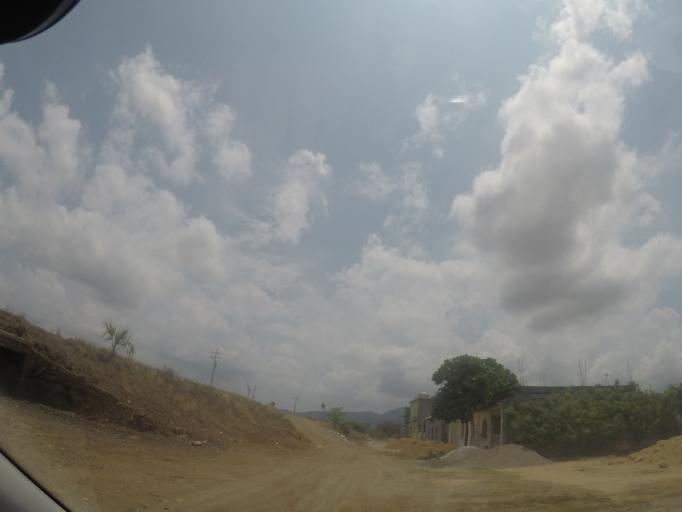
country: MX
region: Oaxaca
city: El Espinal
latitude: 16.5565
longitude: -94.9485
